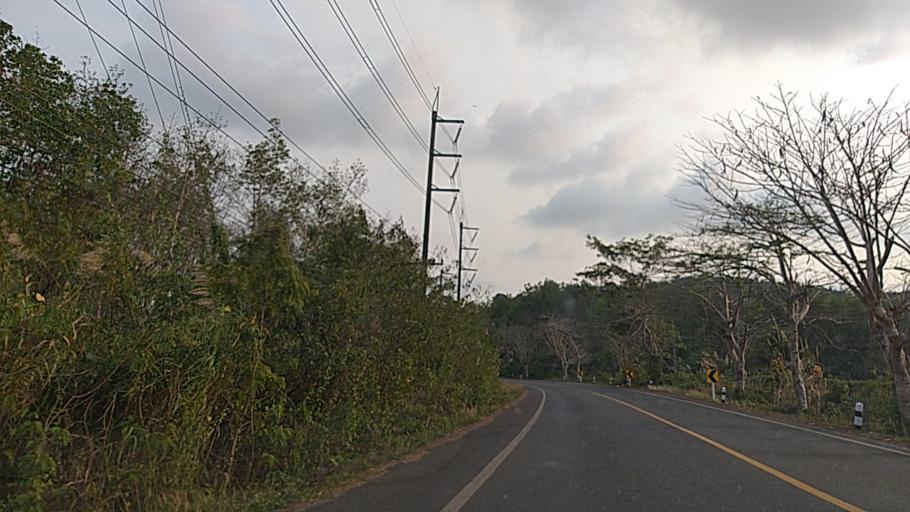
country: TH
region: Trat
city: Laem Ngop
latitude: 12.2761
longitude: 102.3059
